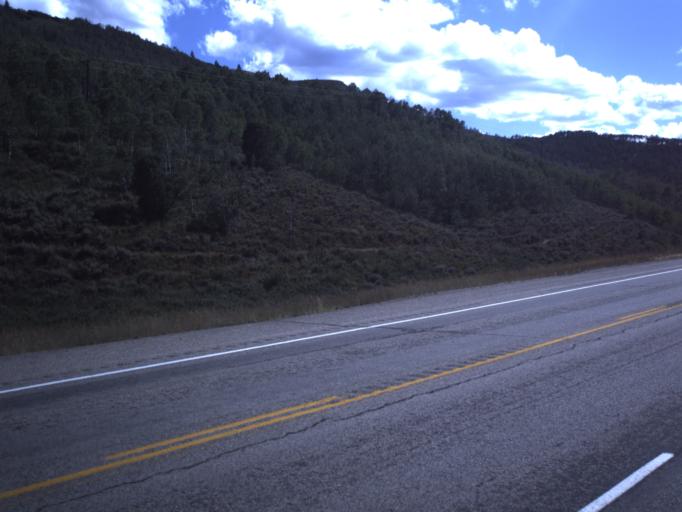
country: US
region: Utah
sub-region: Summit County
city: Francis
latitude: 40.1924
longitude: -111.0126
